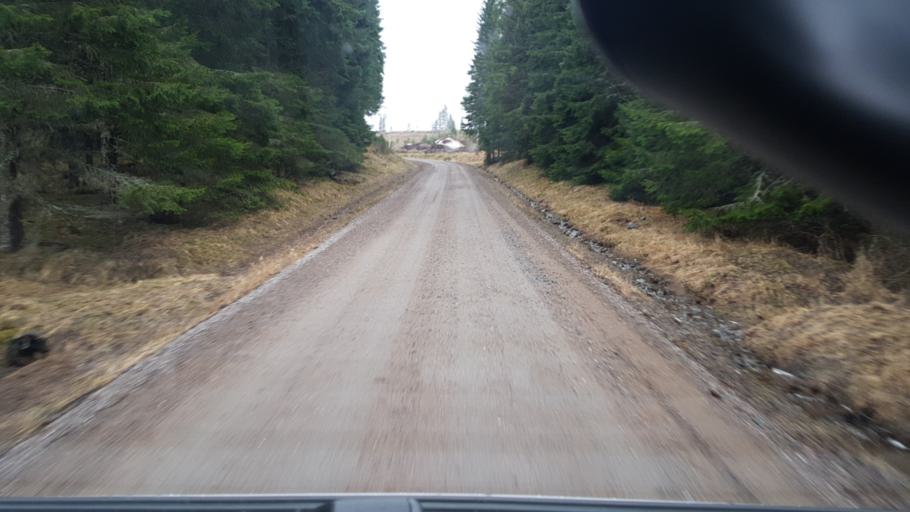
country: SE
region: Vaermland
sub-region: Eda Kommun
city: Charlottenberg
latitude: 60.0373
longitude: 12.5129
